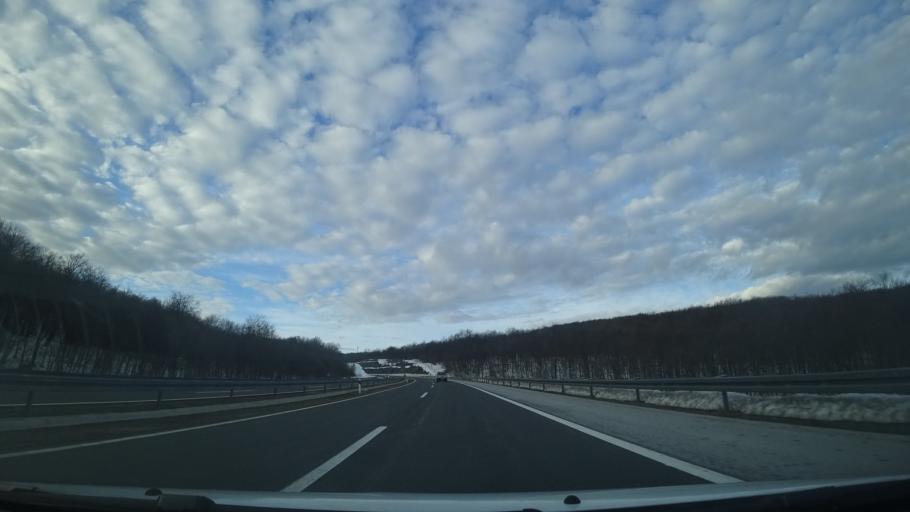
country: HR
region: Karlovacka
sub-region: Grad Ogulin
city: Ogulin
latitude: 45.2736
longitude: 15.2712
